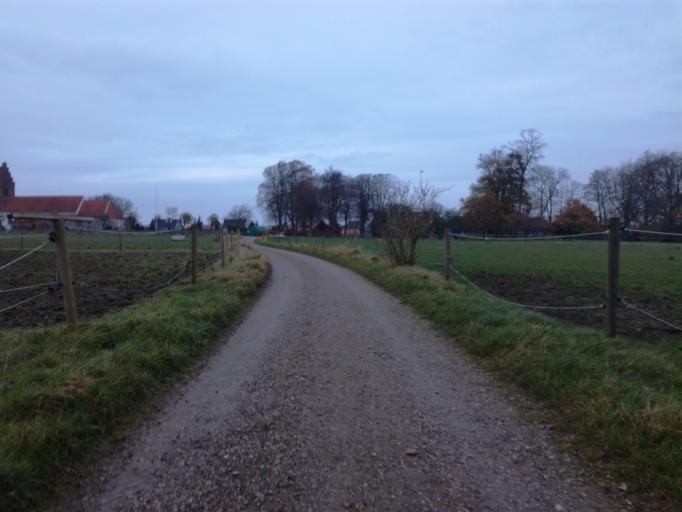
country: DK
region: South Denmark
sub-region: Vejle Kommune
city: Brejning
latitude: 55.6352
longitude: 9.6943
